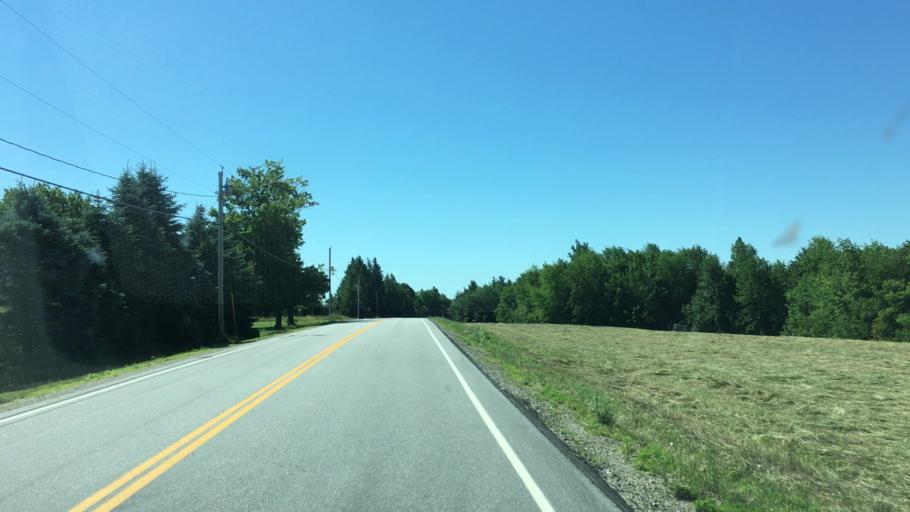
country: US
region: Maine
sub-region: Hancock County
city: Penobscot
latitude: 44.4798
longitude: -68.6389
